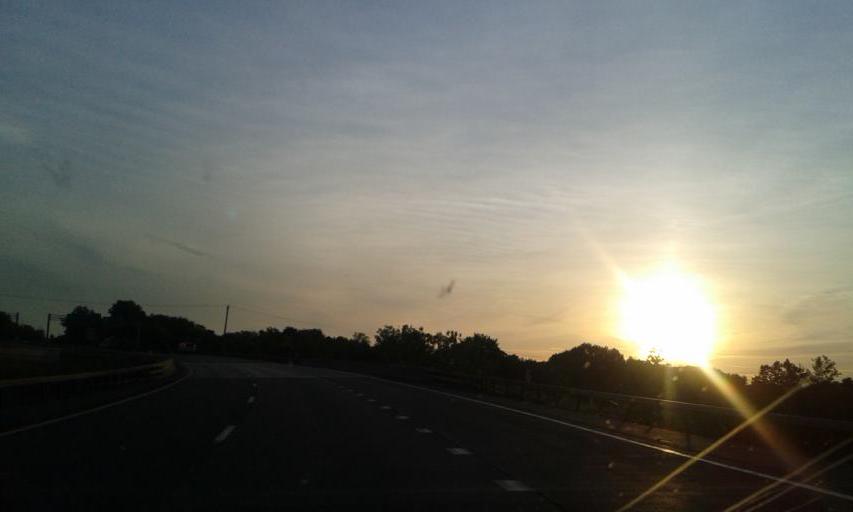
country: US
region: New York
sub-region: Onondaga County
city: Seneca Knolls
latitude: 43.1137
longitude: -76.2693
